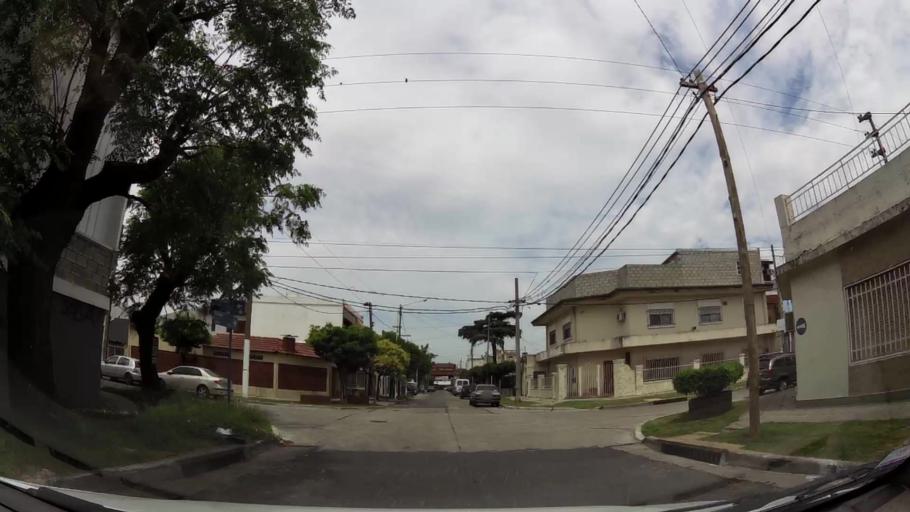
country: AR
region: Buenos Aires
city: San Justo
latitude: -34.6734
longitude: -58.5341
